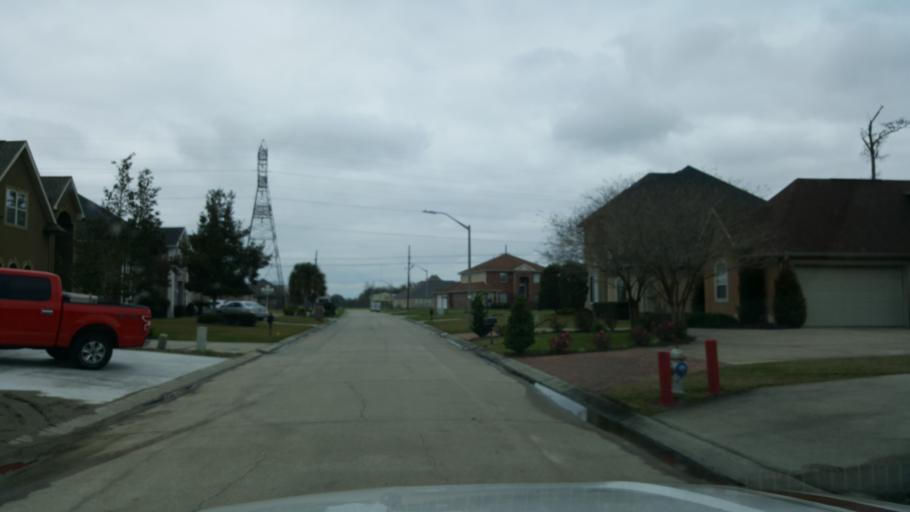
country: US
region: Louisiana
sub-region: Jefferson Parish
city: Woodmere
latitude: 29.8790
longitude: -90.0817
